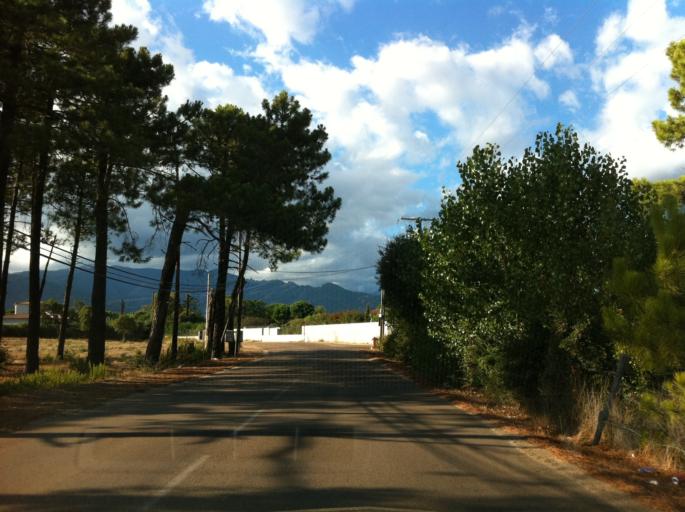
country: FR
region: Corsica
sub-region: Departement de la Corse-du-Sud
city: Porto-Vecchio
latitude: 41.6414
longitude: 9.3330
